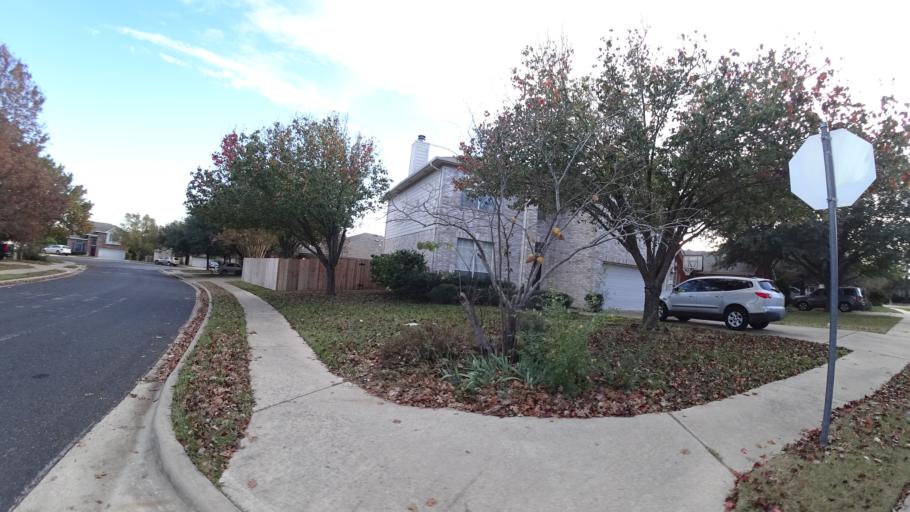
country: US
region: Texas
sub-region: Williamson County
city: Brushy Creek
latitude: 30.5009
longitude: -97.7299
